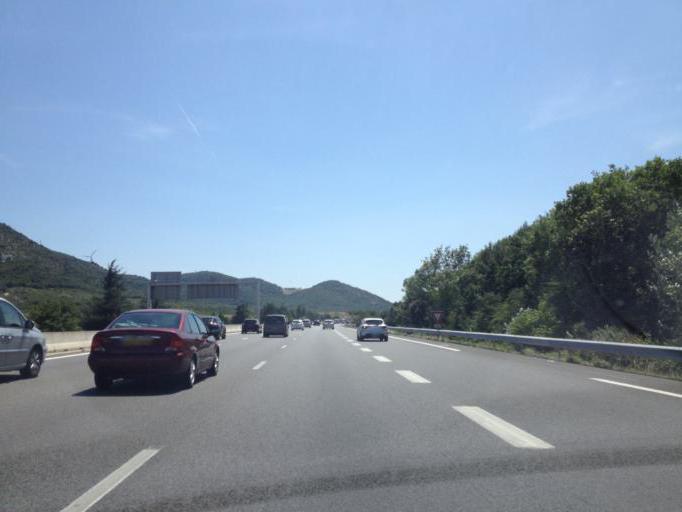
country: FR
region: Rhone-Alpes
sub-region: Departement de la Drome
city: Malataverne
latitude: 44.4774
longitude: 4.7666
